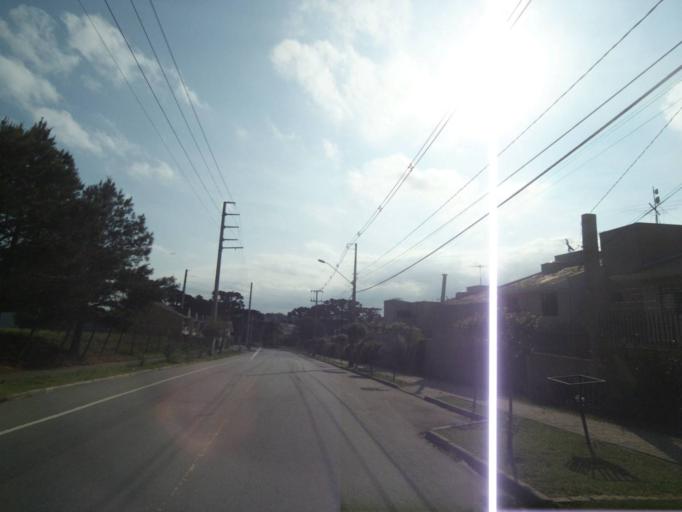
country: BR
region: Parana
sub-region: Pinhais
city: Pinhais
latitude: -25.4097
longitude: -49.2154
